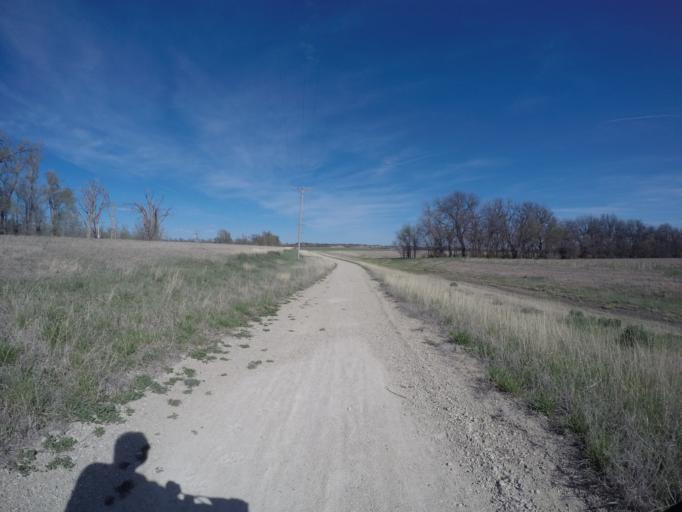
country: US
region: Kansas
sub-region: Saline County
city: Salina
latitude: 38.7834
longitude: -97.5908
